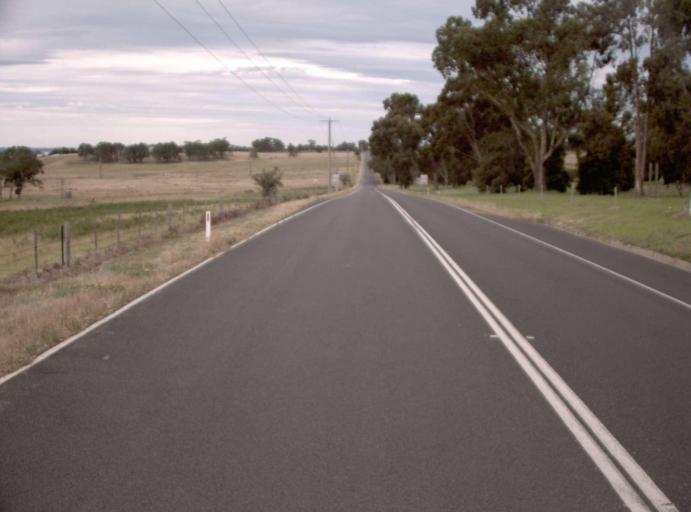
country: AU
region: Victoria
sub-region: East Gippsland
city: Bairnsdale
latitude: -37.9024
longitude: 147.6844
